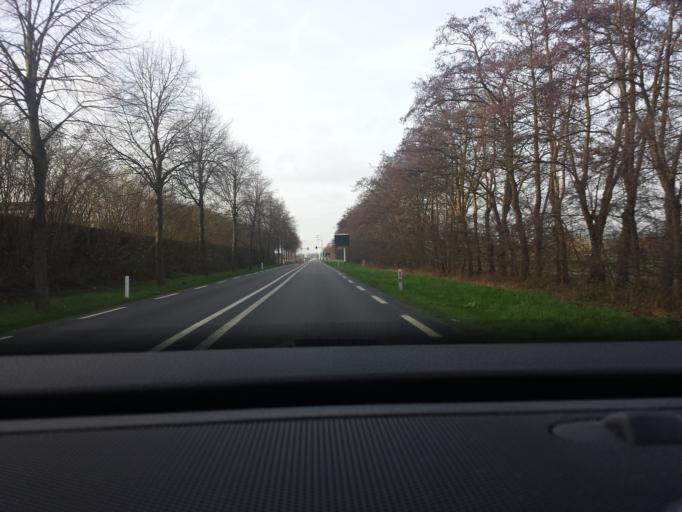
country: NL
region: Gelderland
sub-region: Gemeente Duiven
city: Duiven
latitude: 51.9548
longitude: 6.0319
